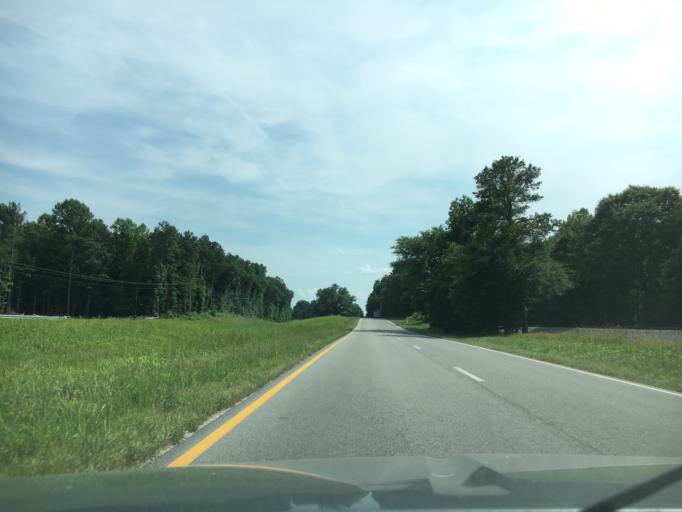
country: US
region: Virginia
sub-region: Nottoway County
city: Crewe
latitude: 37.2469
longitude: -78.1429
